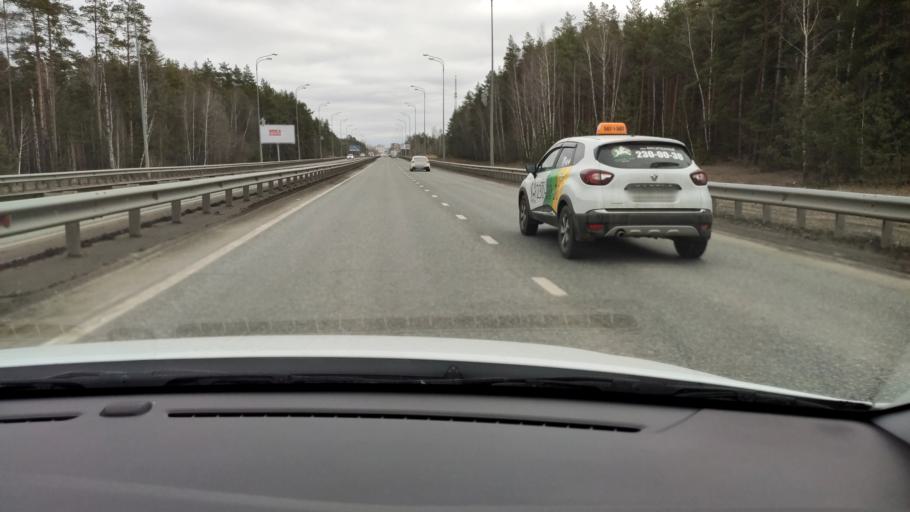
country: RU
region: Tatarstan
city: Staroye Arakchino
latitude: 55.8287
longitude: 49.0026
